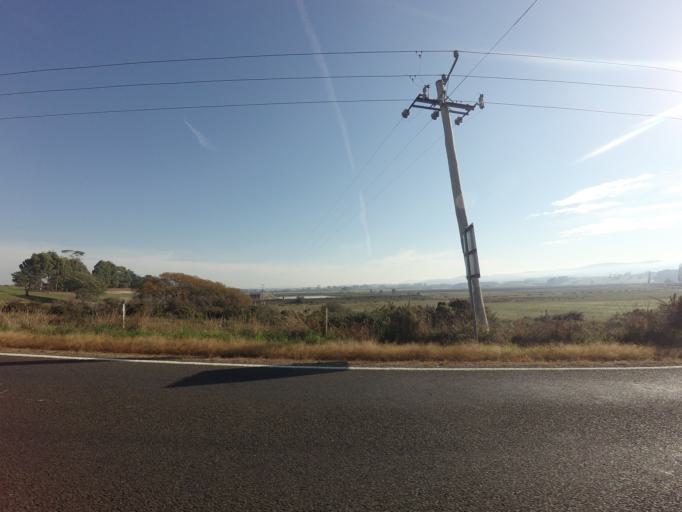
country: AU
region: Tasmania
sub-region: Launceston
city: Summerhill
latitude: -41.5283
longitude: 147.0190
